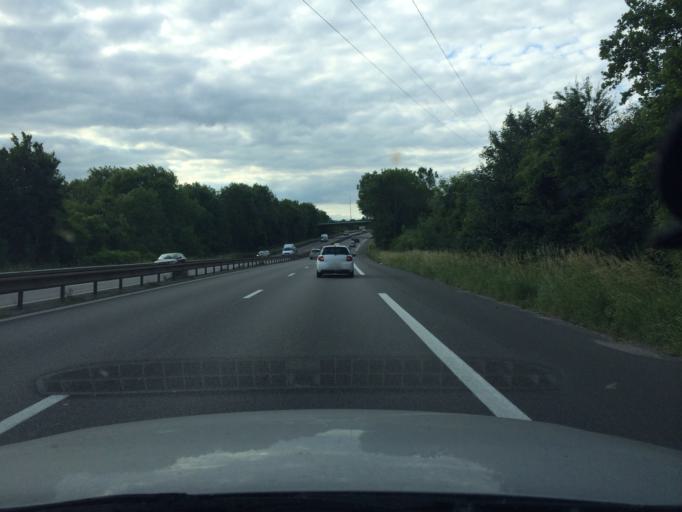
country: FR
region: Lorraine
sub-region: Departement de Meurthe-et-Moselle
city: Chavigny
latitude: 48.6542
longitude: 6.1285
